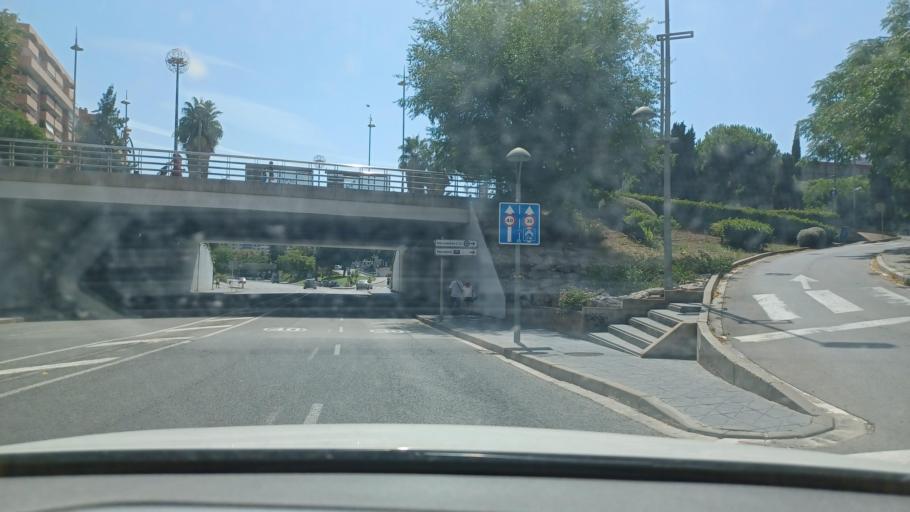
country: ES
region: Catalonia
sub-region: Provincia de Tarragona
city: Tarragona
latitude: 41.1184
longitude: 1.2396
